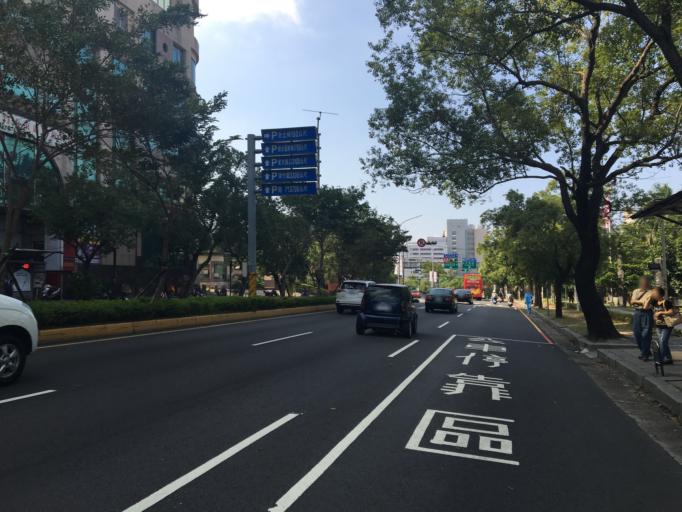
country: TW
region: Taiwan
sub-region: Hsinchu
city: Hsinchu
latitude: 24.7982
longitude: 120.9949
